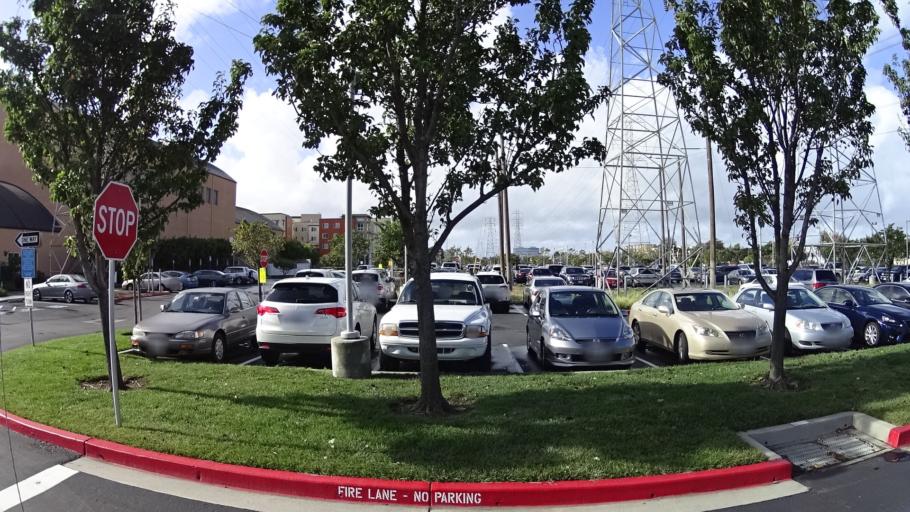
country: US
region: California
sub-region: San Mateo County
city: Foster City
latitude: 37.5585
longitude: -122.2654
